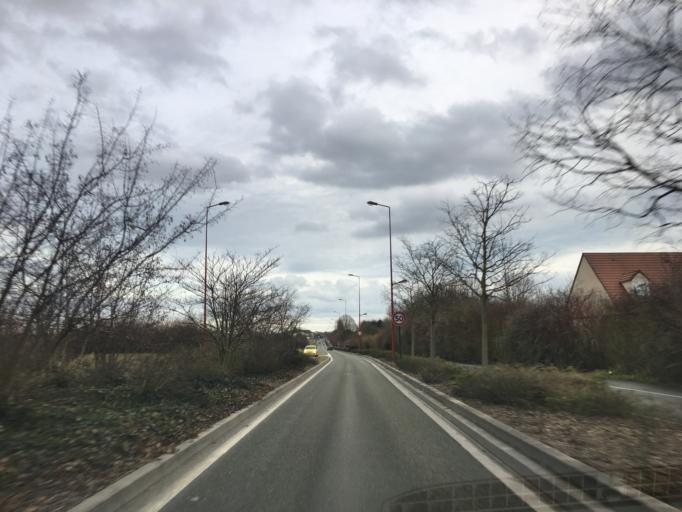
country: FR
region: Ile-de-France
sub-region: Departement du Val-d'Oise
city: Gonesse
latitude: 48.9987
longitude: 2.4344
